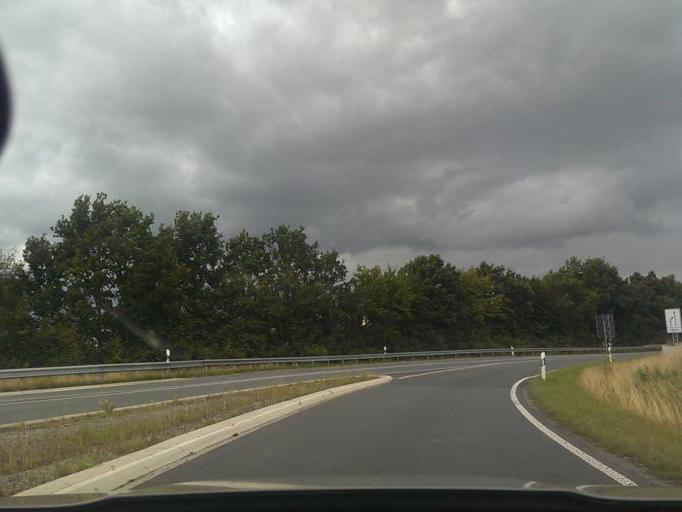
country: DE
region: North Rhine-Westphalia
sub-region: Regierungsbezirk Detmold
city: Steinheim
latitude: 51.8658
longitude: 9.1075
